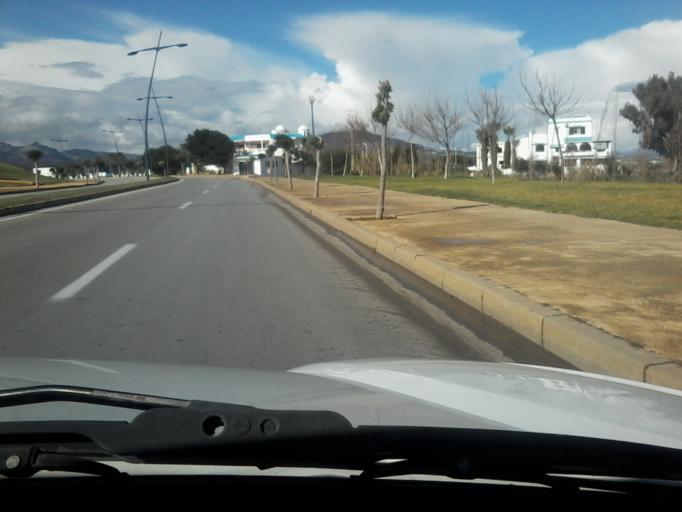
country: MA
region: Tanger-Tetouan
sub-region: Tetouan
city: Martil
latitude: 35.6944
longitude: -5.3335
